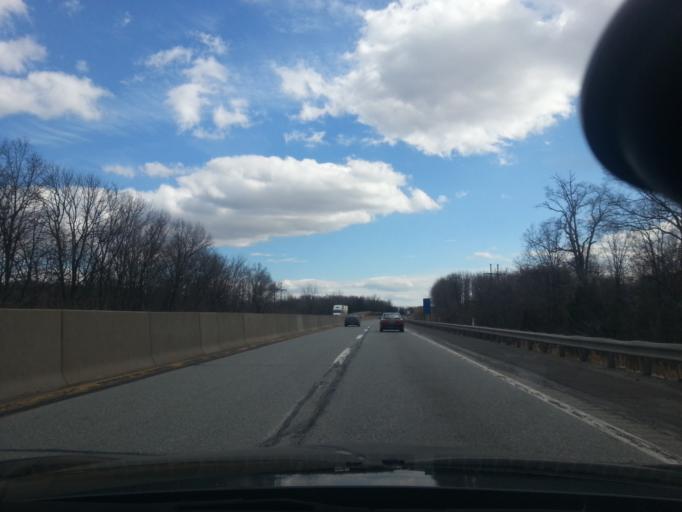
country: US
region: Pennsylvania
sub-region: Bucks County
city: Spinnerstown
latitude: 40.4305
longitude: -75.4207
